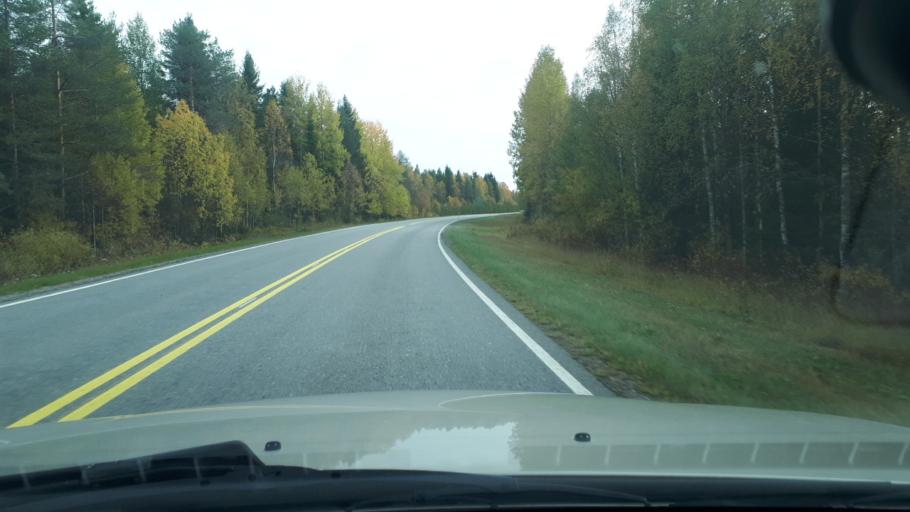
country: FI
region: Lapland
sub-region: Rovaniemi
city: Ranua
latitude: 66.0015
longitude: 26.2280
